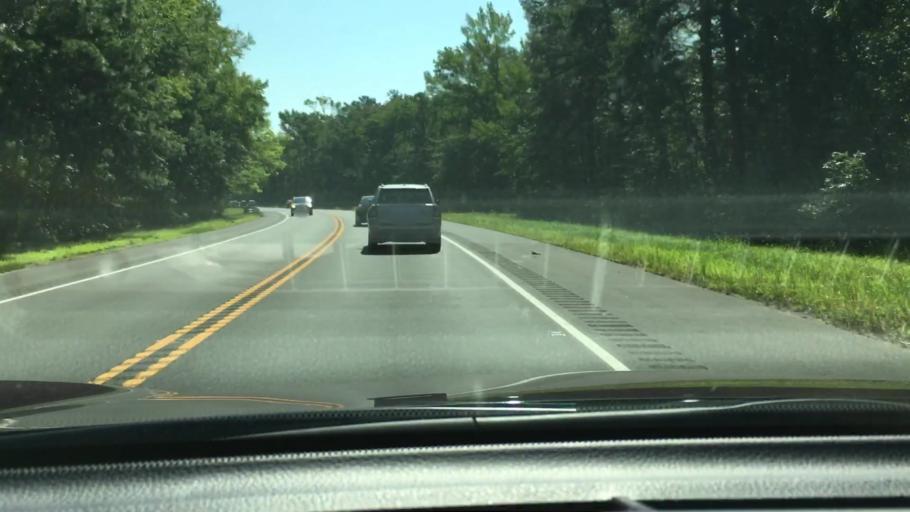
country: US
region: New Jersey
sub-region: Cape May County
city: Woodbine
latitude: 39.3246
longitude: -74.8654
